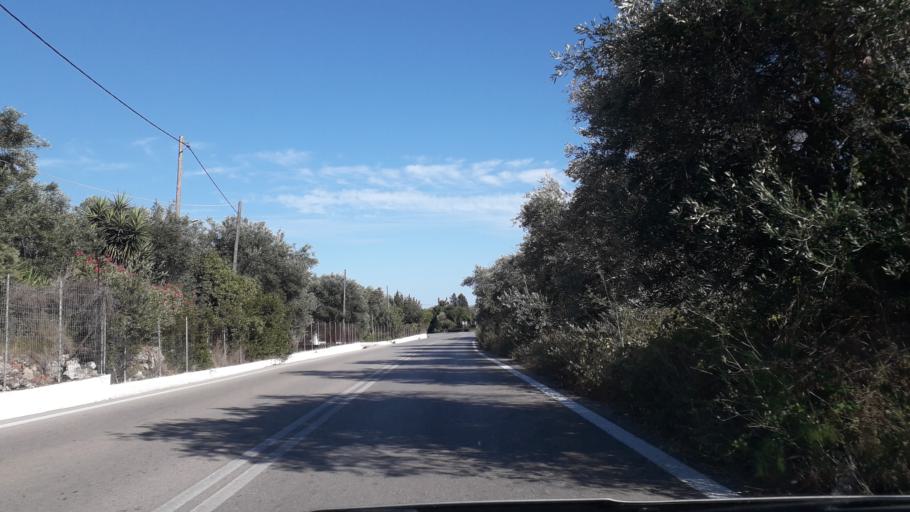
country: GR
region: Ionian Islands
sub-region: Nomos Kerkyras
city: Agios Matthaios
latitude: 39.4562
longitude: 19.9190
